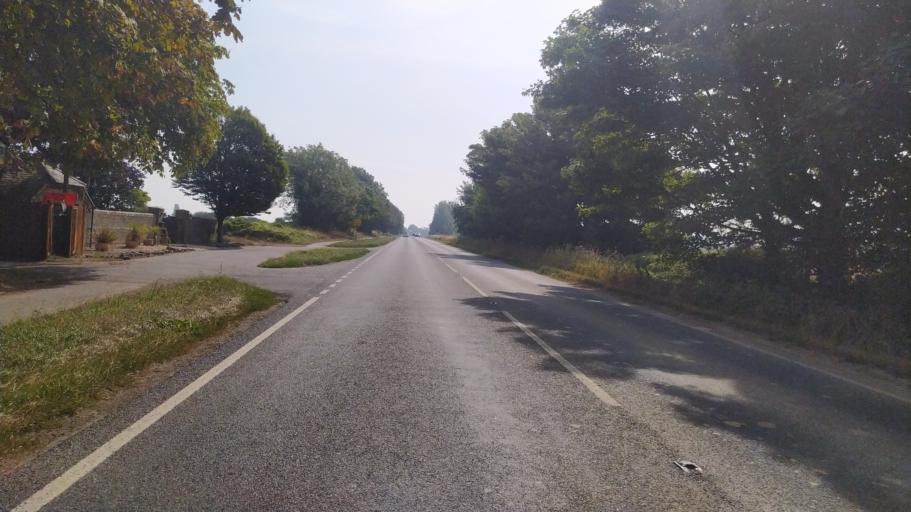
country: GB
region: England
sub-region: West Sussex
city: Boxgrove
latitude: 50.8229
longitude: -0.7281
